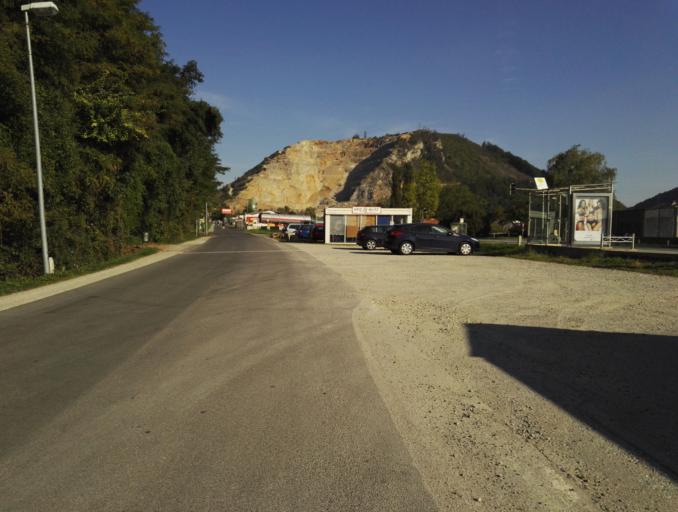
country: AT
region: Styria
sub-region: Politischer Bezirk Graz-Umgebung
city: Gratkorn
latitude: 47.1218
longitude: 15.3632
